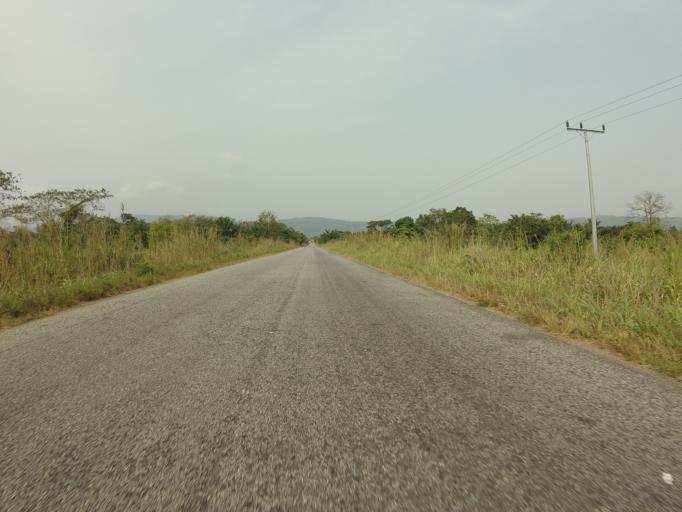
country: GH
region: Volta
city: Ho
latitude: 6.5746
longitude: 0.3400
